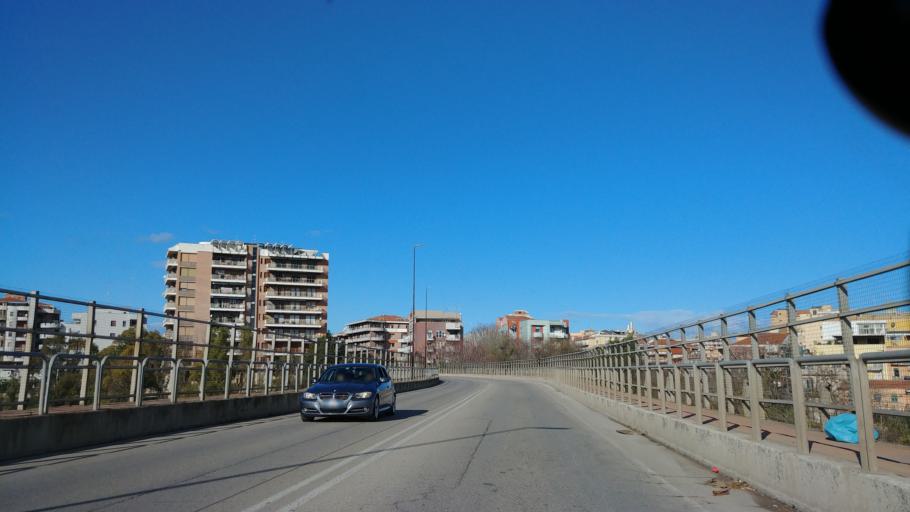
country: IT
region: Molise
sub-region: Provincia di Campobasso
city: Termoli
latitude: 41.9956
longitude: 14.9968
